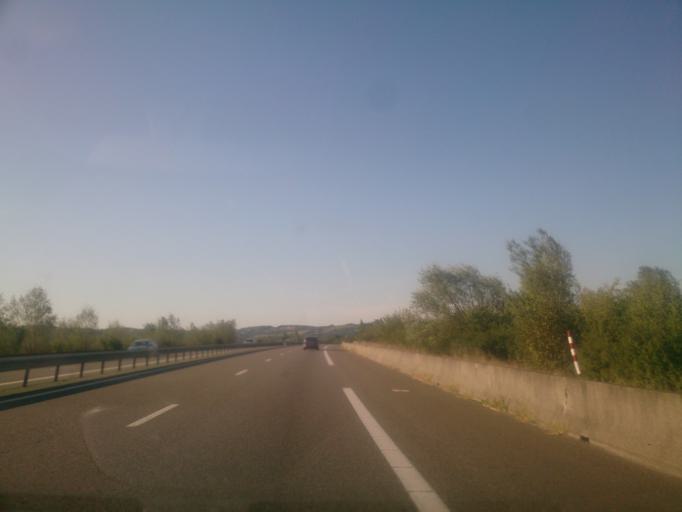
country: FR
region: Midi-Pyrenees
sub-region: Departement du Tarn-et-Garonne
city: Albias
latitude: 44.0734
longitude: 1.4206
